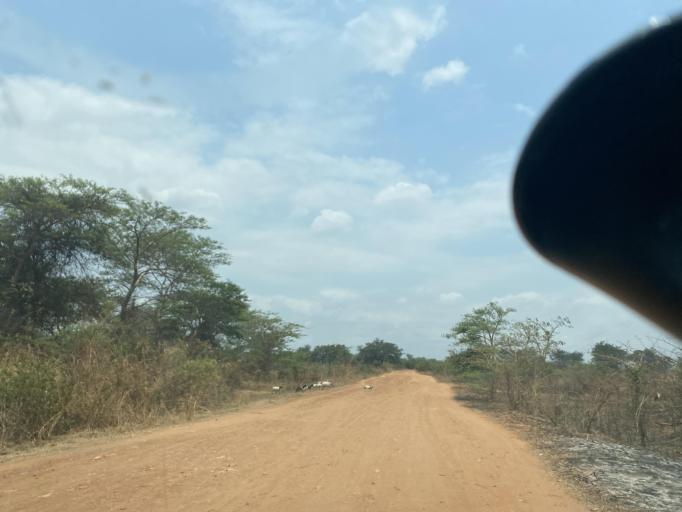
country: ZM
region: Lusaka
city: Chongwe
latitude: -15.5177
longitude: 28.8205
